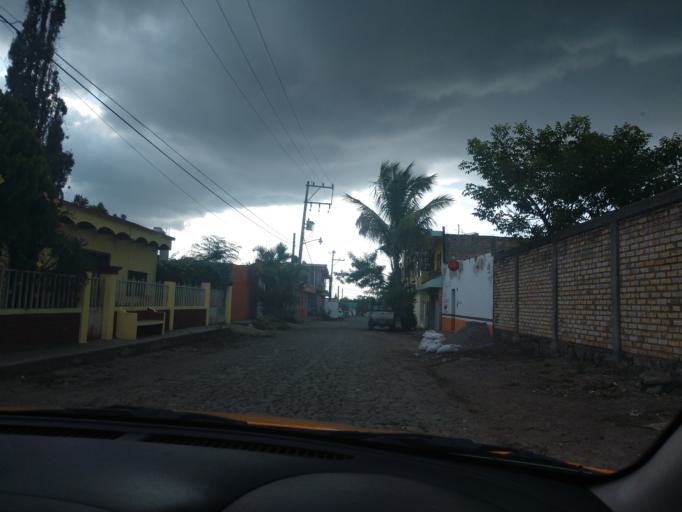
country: MX
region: Nayarit
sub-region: Tepic
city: La Corregidora
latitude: 21.4505
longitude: -104.8144
